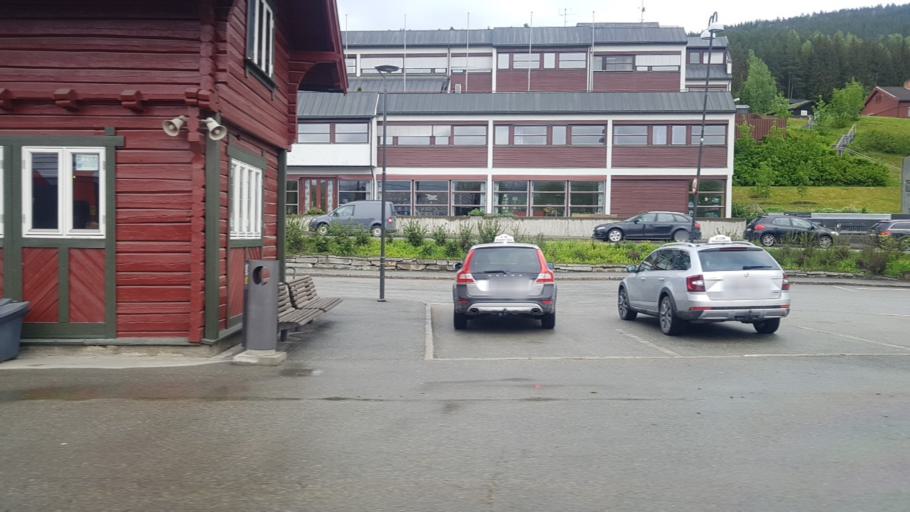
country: NO
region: Oppland
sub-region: Nord-Fron
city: Vinstra
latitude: 61.5987
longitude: 9.7341
